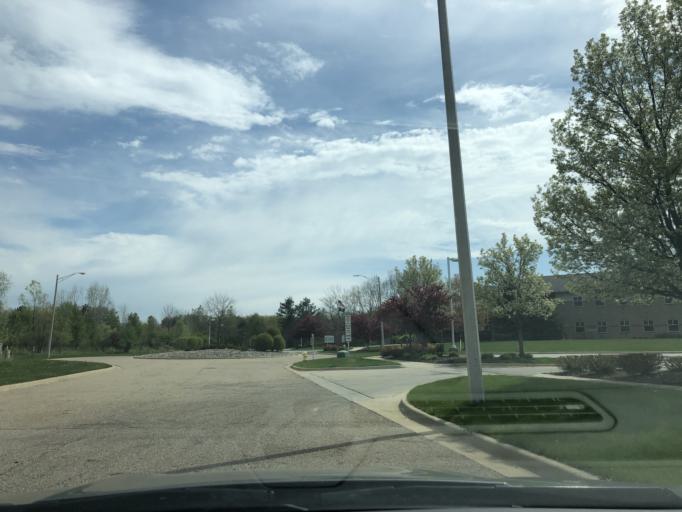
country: US
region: Michigan
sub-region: Eaton County
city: Waverly
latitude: 42.7217
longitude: -84.6487
